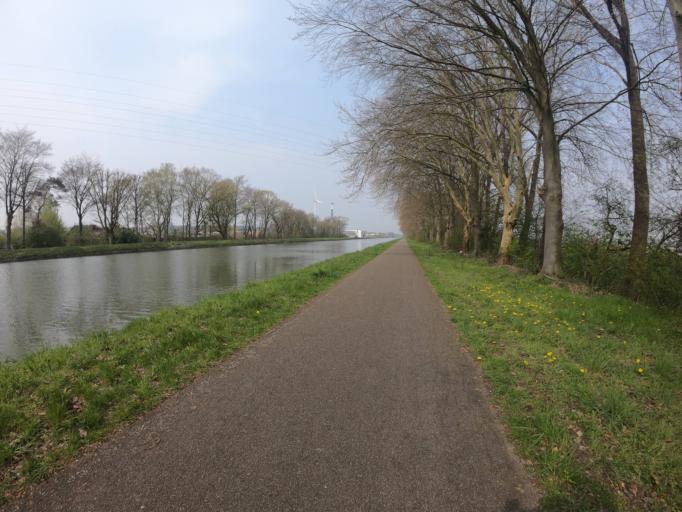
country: NL
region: Limburg
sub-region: Gemeente Stein
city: Berg
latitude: 51.0408
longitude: 5.7044
